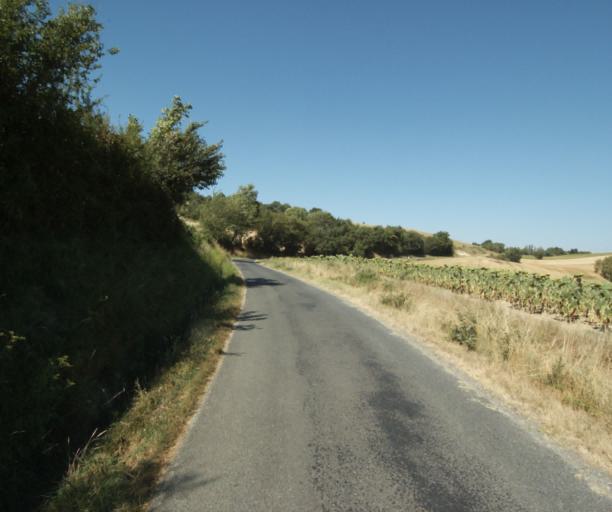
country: FR
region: Midi-Pyrenees
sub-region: Departement de la Haute-Garonne
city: Saint-Felix-Lauragais
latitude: 43.5064
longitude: 1.9378
